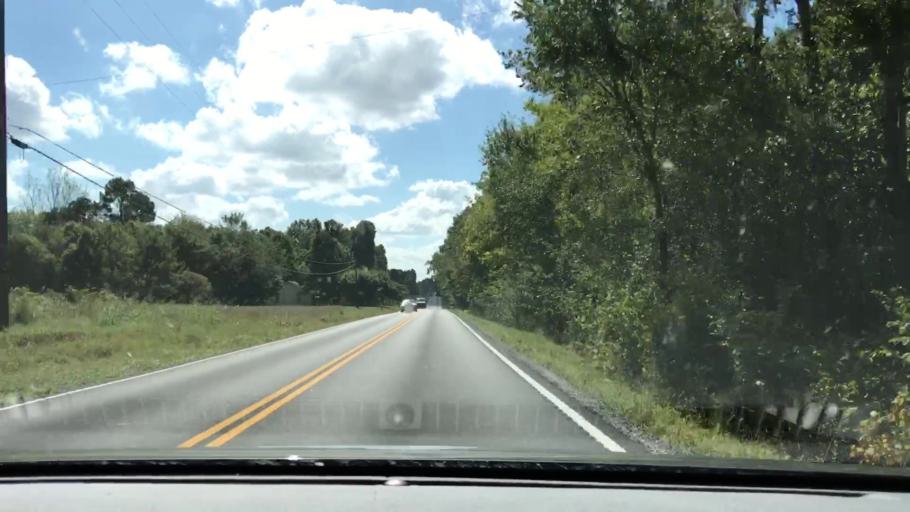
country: US
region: Kentucky
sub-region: Graves County
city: Mayfield
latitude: 36.7951
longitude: -88.5955
